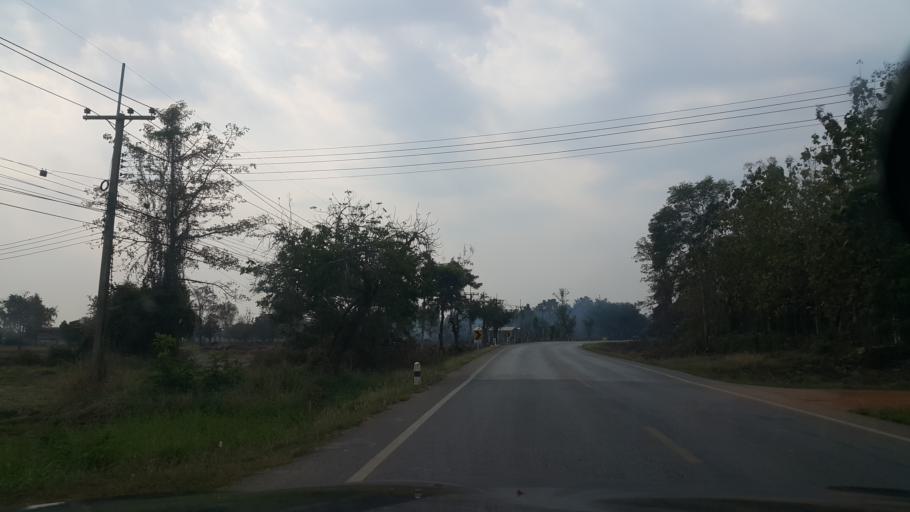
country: TH
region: Sukhothai
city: Si Samrong
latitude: 17.1083
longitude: 99.8891
